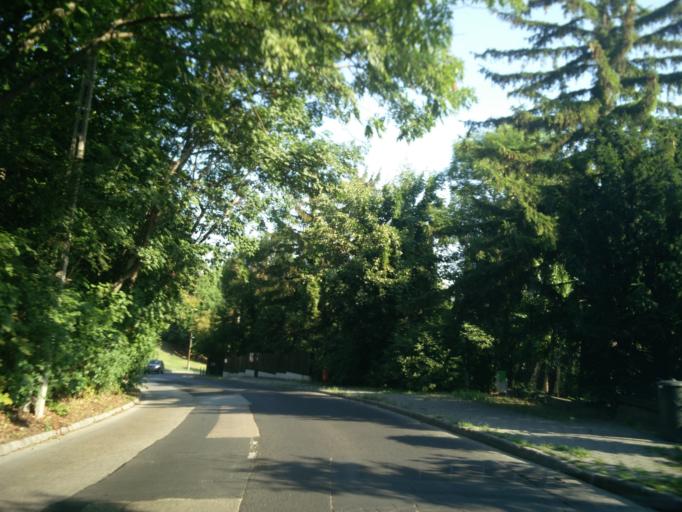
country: HU
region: Budapest
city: Budapest XII. keruelet
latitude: 47.5059
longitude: 18.9822
